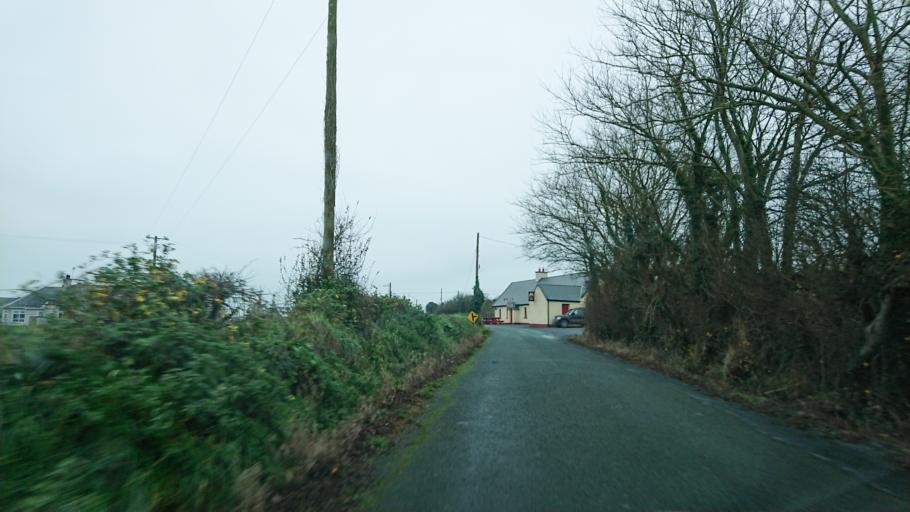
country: IE
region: Munster
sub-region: Waterford
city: Dunmore East
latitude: 52.1453
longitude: -7.0568
